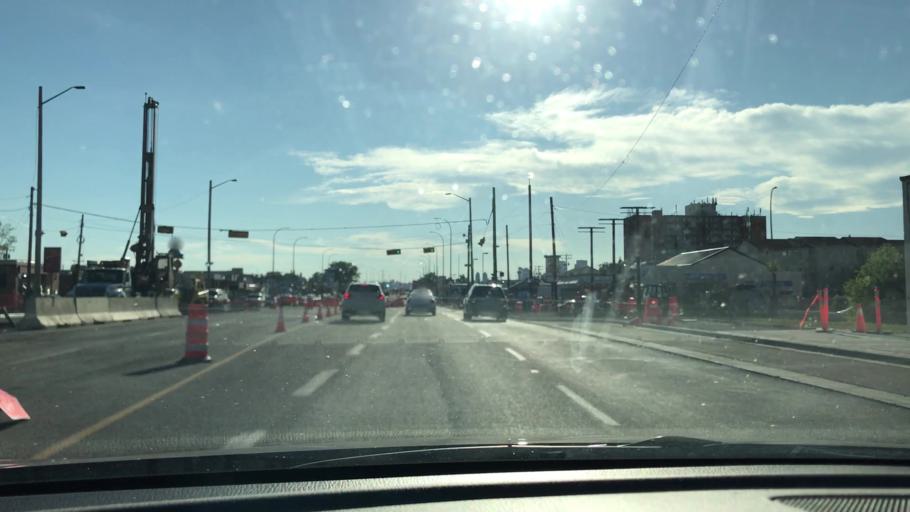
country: CA
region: Alberta
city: Calgary
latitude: 51.0380
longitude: -113.9804
